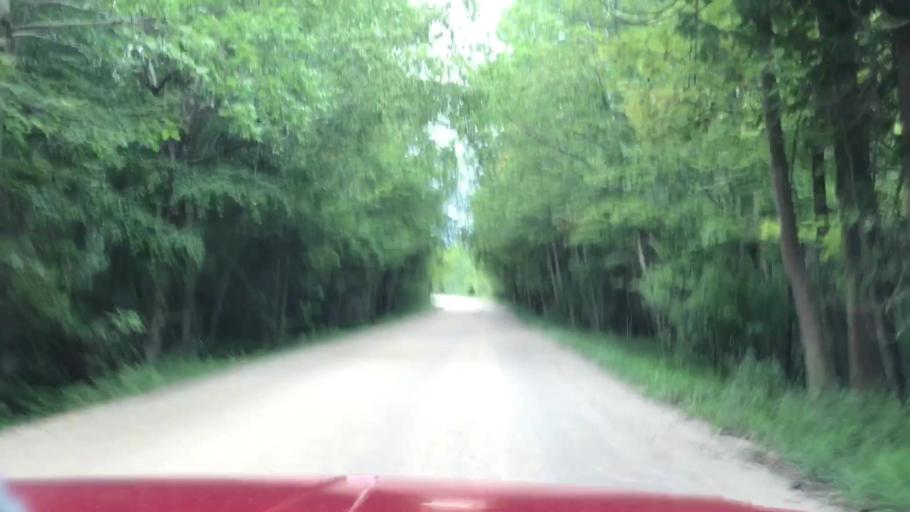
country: US
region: Michigan
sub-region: Charlevoix County
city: Charlevoix
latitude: 45.7286
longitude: -85.5399
